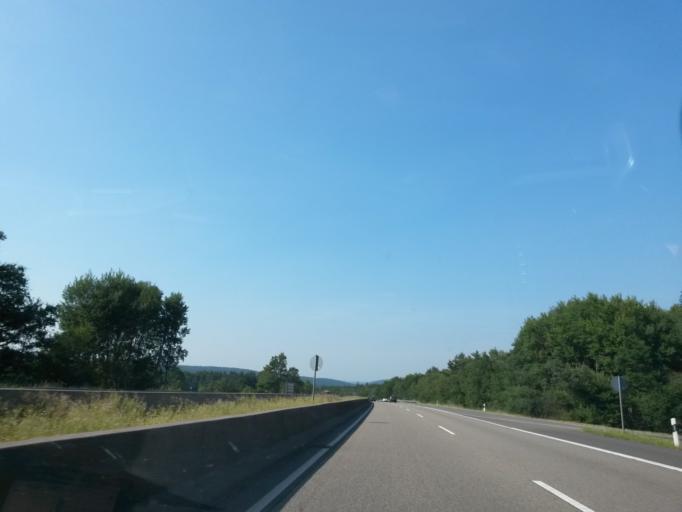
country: DE
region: Hesse
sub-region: Regierungsbezirk Kassel
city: Burghaun
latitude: 50.6849
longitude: 9.6832
